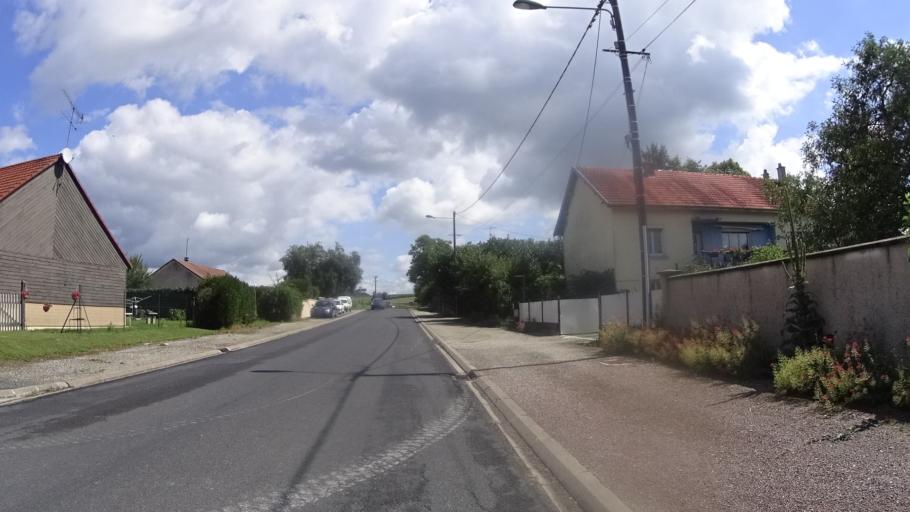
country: FR
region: Champagne-Ardenne
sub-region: Departement de la Haute-Marne
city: Montier-en-Der
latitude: 48.4565
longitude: 4.7010
